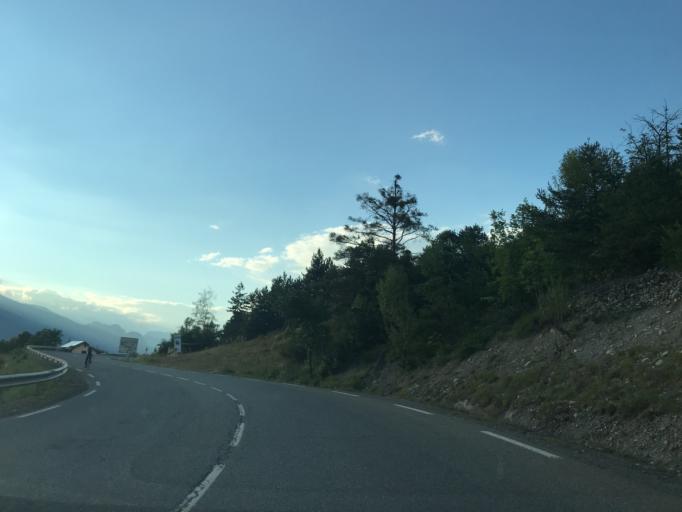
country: FR
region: Provence-Alpes-Cote d'Azur
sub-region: Departement des Hautes-Alpes
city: Guillestre
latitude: 44.6543
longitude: 6.6550
